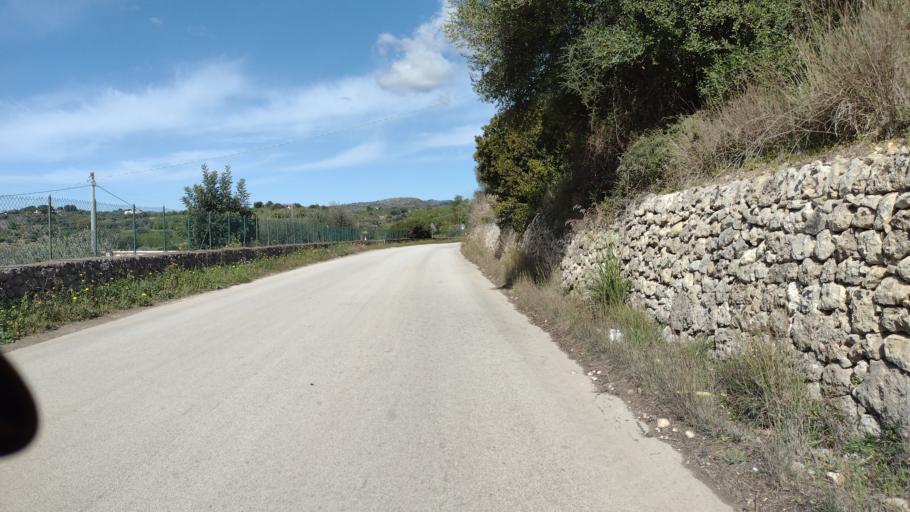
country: IT
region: Sicily
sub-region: Provincia di Siracusa
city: Noto
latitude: 36.8908
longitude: 15.0446
